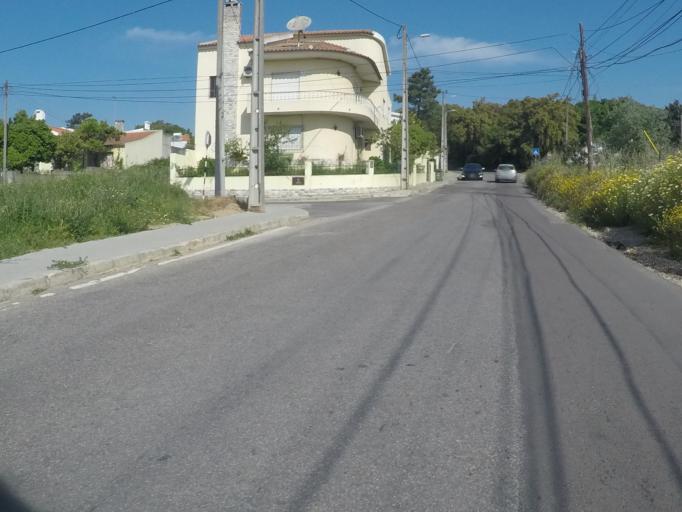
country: PT
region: Setubal
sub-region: Seixal
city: Amora
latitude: 38.6086
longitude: -9.1222
